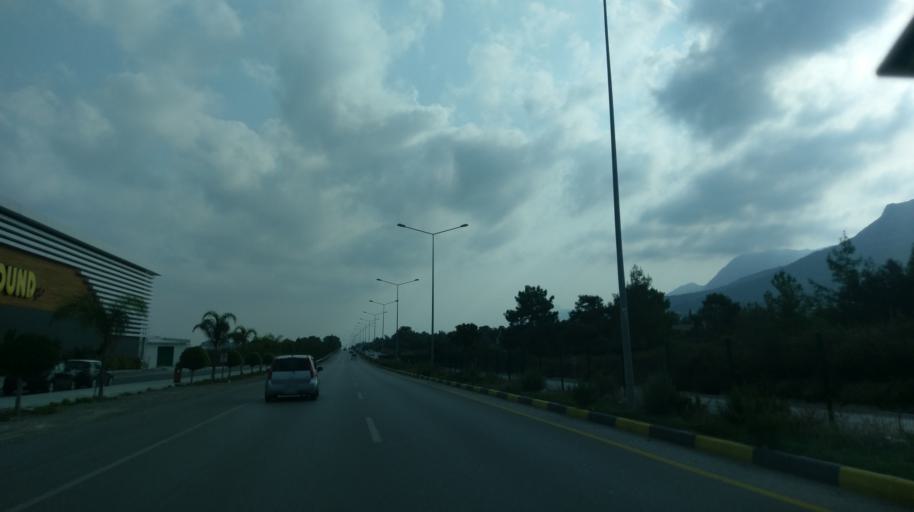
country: CY
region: Keryneia
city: Kyrenia
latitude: 35.3289
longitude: 33.2861
